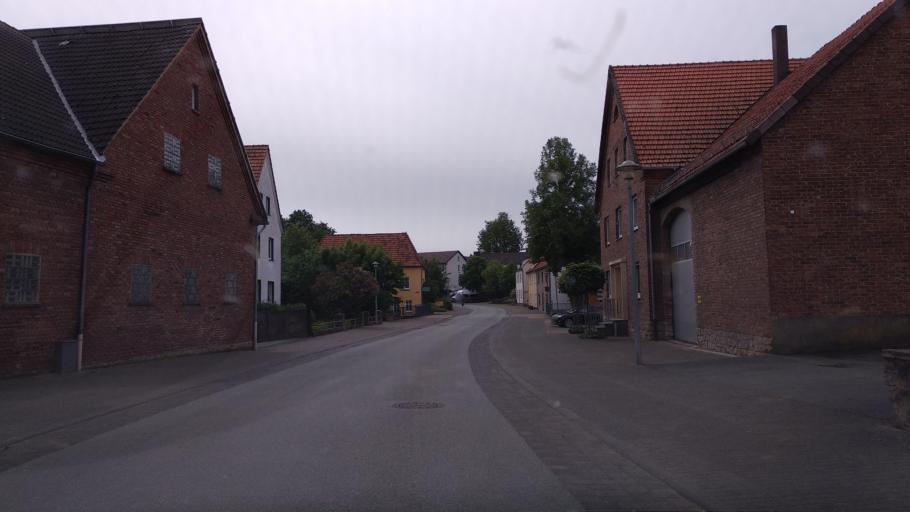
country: DE
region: North Rhine-Westphalia
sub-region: Regierungsbezirk Detmold
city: Willebadessen
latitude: 51.5967
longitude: 9.1292
